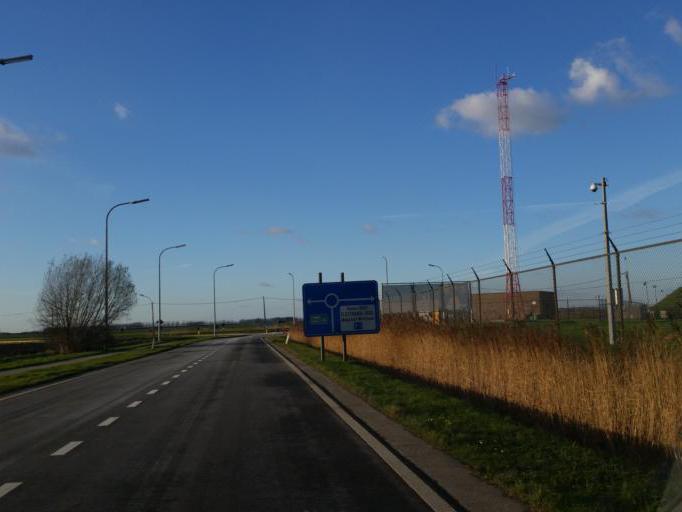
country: BE
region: Flanders
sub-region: Provincie Oost-Vlaanderen
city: Beveren
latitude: 51.3211
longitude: 4.2511
